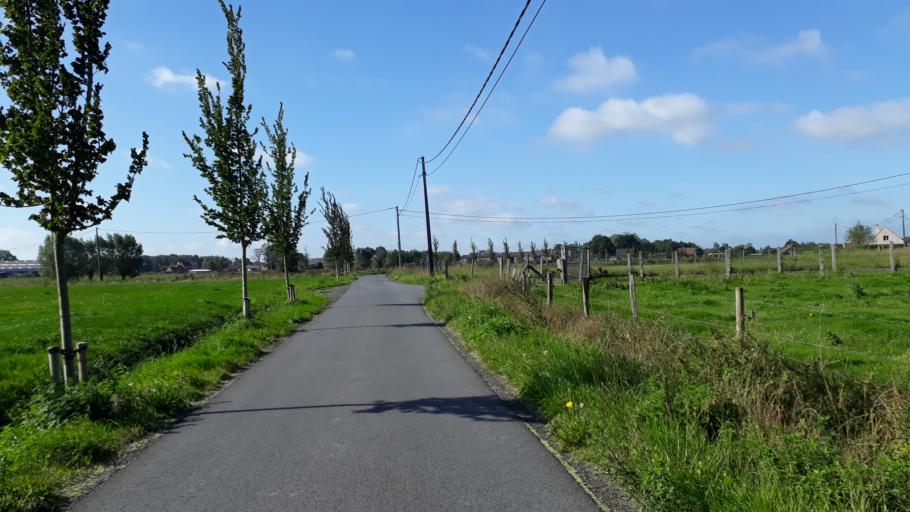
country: BE
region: Flanders
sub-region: Provincie West-Vlaanderen
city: Lichtervelde
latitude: 51.0666
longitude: 3.1370
